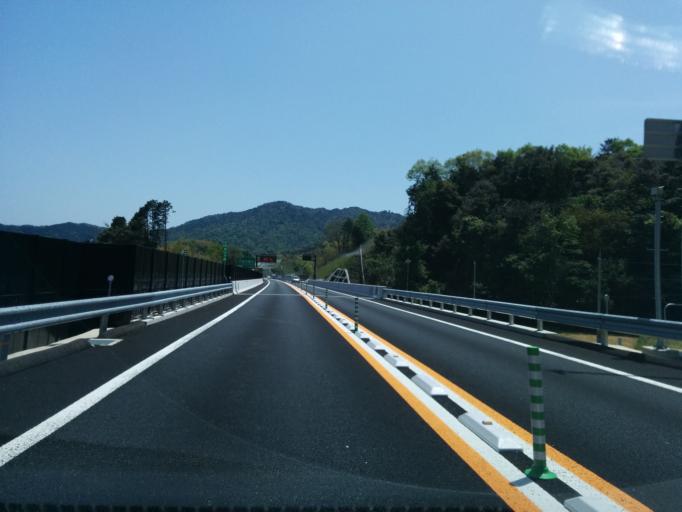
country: JP
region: Kyoto
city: Miyazu
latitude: 35.5528
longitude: 135.1341
